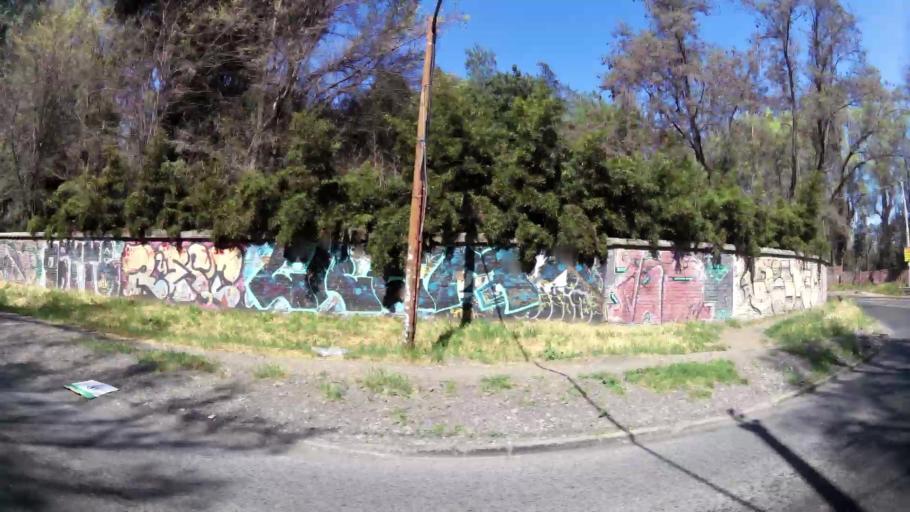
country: CL
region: Santiago Metropolitan
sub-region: Provincia de Santiago
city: Villa Presidente Frei, Nunoa, Santiago, Chile
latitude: -33.4963
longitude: -70.5715
